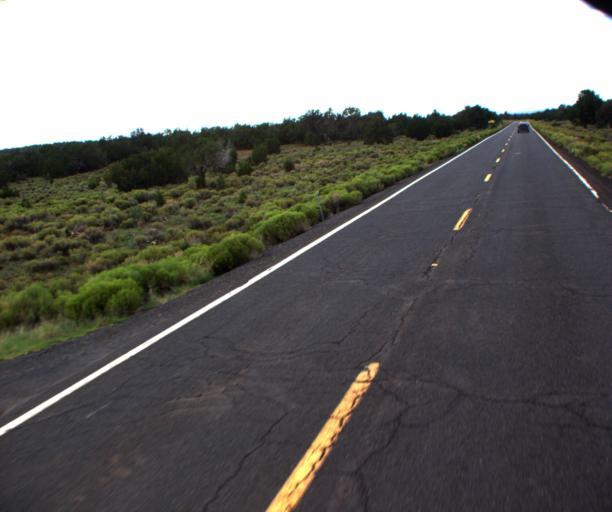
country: US
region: Arizona
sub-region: Coconino County
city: Parks
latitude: 35.5378
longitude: -111.8526
